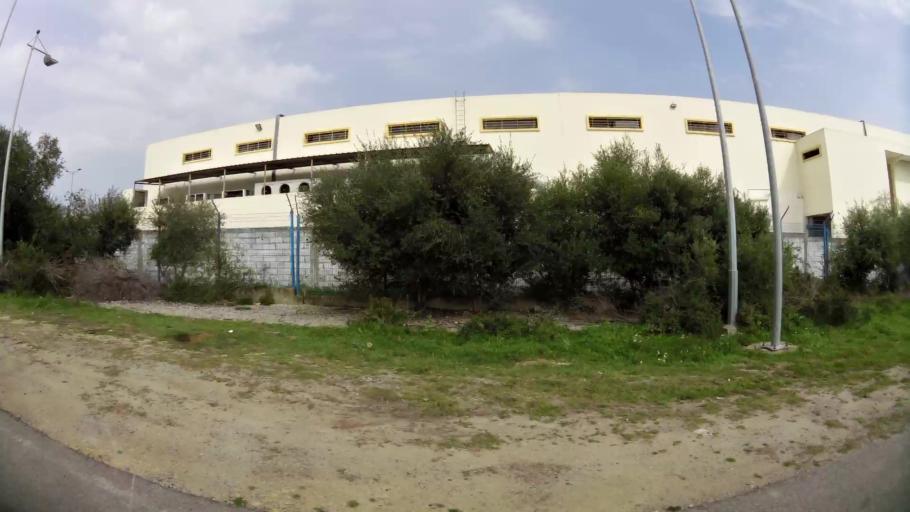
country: MA
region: Tanger-Tetouan
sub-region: Tanger-Assilah
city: Boukhalef
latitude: 35.7271
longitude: -5.9021
